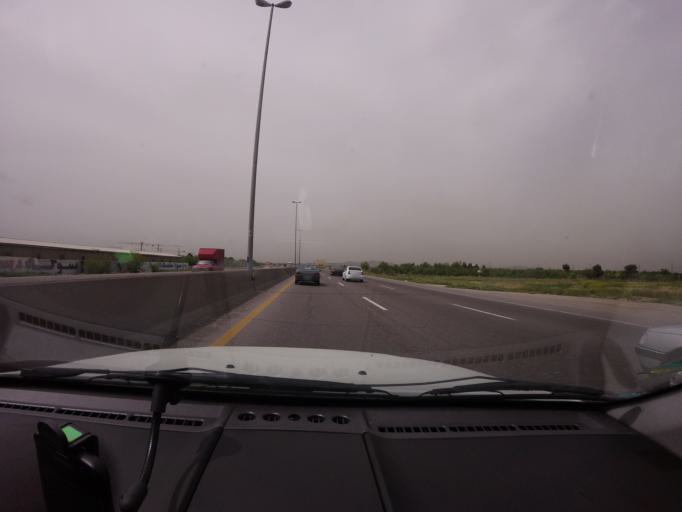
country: IR
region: Tehran
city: Robat Karim
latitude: 35.5275
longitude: 51.0874
